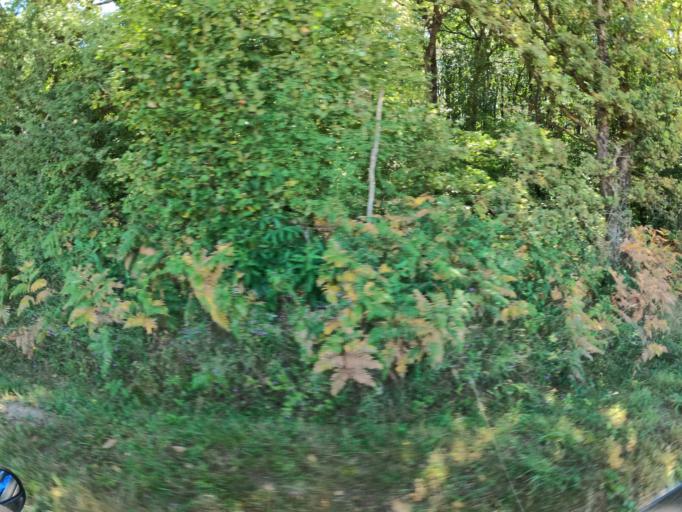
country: FR
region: Pays de la Loire
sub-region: Departement de la Loire-Atlantique
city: La Limouziniere
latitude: 46.9437
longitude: -1.6221
